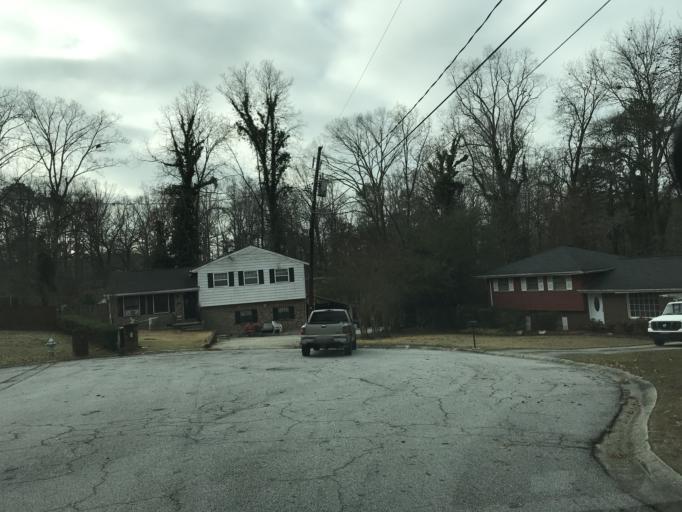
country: US
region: Georgia
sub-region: Clayton County
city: Riverdale
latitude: 33.5609
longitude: -84.3751
